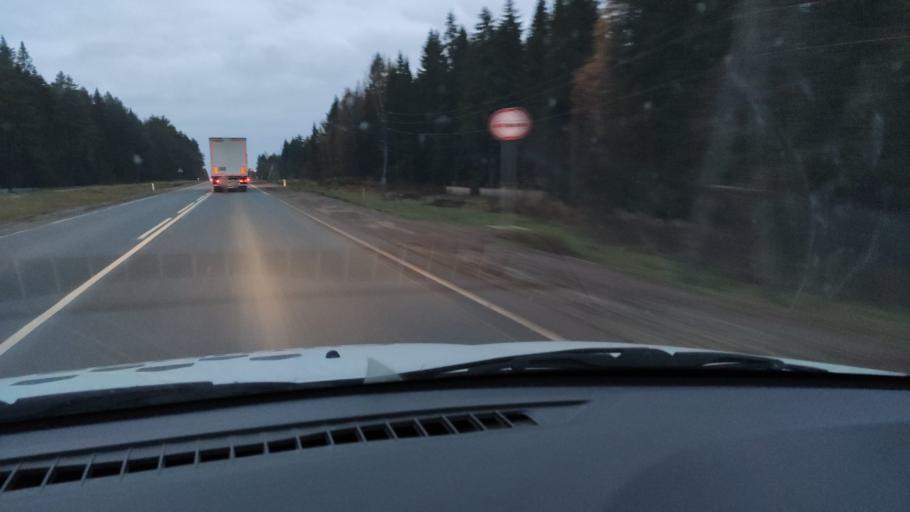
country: RU
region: Kirov
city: Kostino
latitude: 58.8417
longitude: 53.3021
